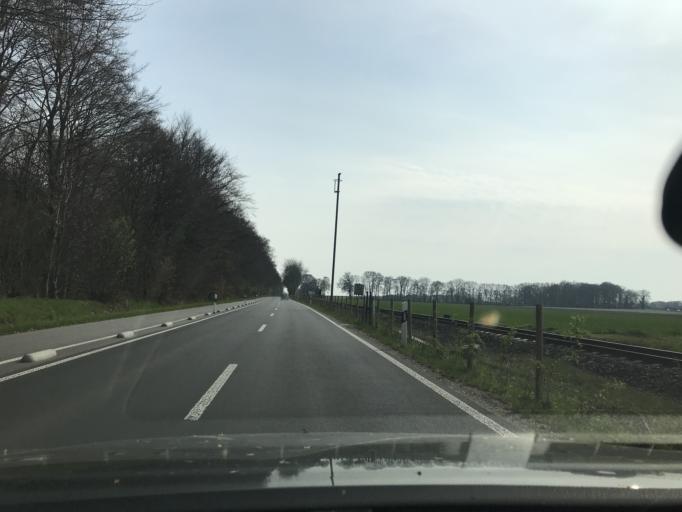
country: DE
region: North Rhine-Westphalia
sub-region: Regierungsbezirk Dusseldorf
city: Kleve
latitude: 51.7403
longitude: 6.1676
